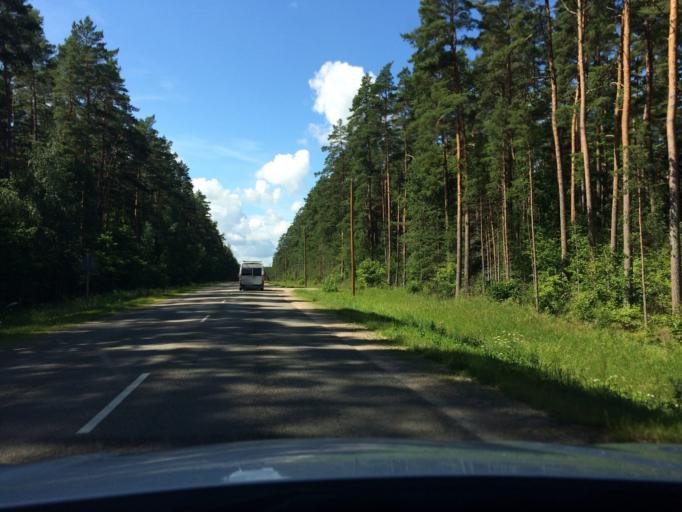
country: LV
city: Tervete
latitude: 56.4887
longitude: 23.4327
